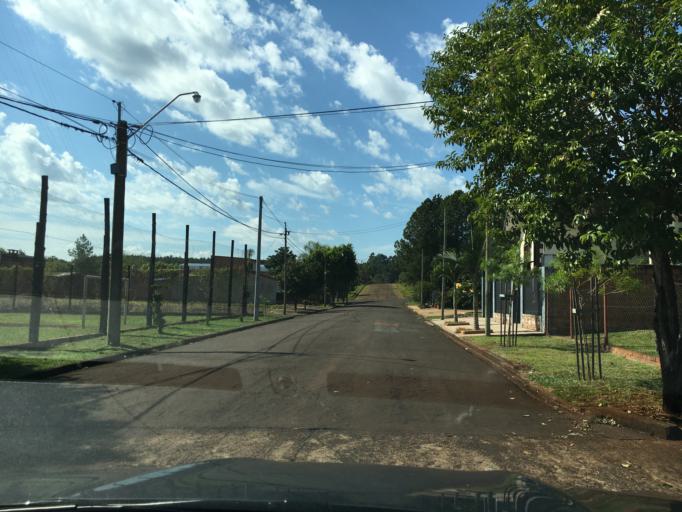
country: AR
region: Misiones
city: Puerto Rico
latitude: -26.8168
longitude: -55.0194
